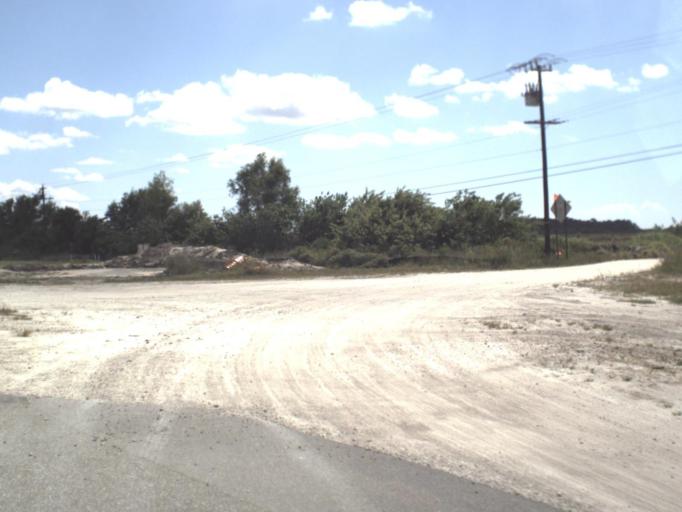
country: US
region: Florida
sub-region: Collier County
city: Lely Resort
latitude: 26.0332
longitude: -81.6520
